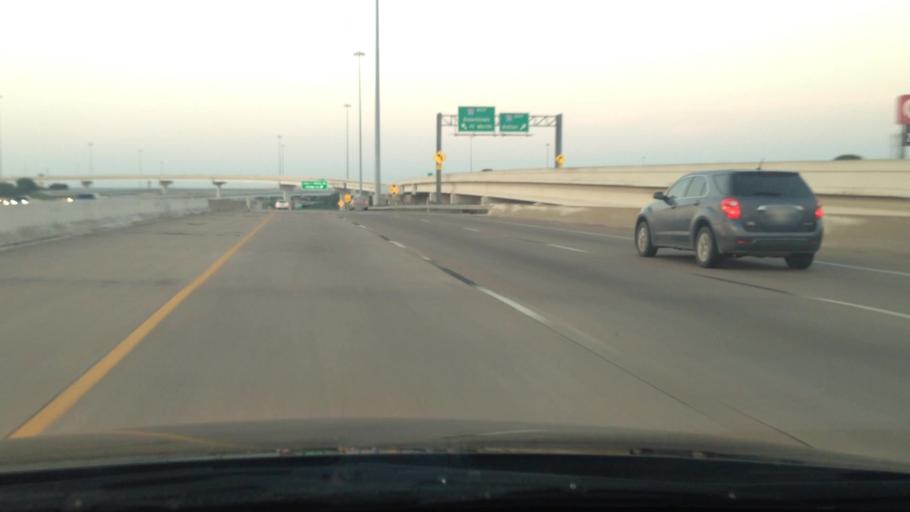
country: US
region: Texas
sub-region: Tarrant County
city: Richland Hills
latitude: 32.7543
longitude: -97.2167
